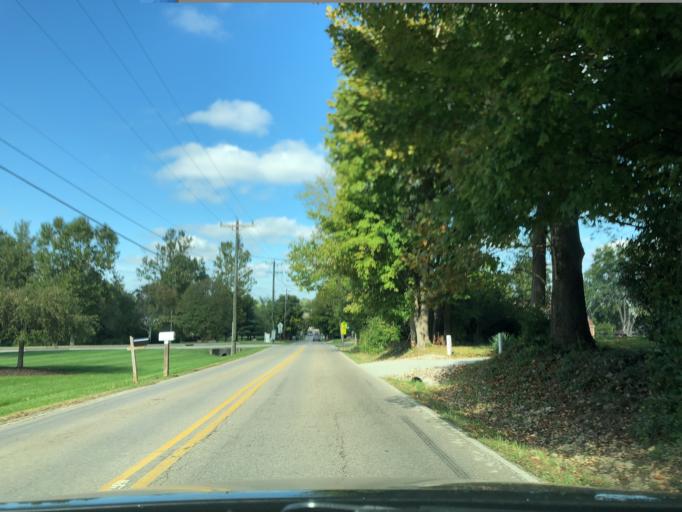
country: US
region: Ohio
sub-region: Hamilton County
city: Loveland
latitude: 39.2539
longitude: -84.2503
